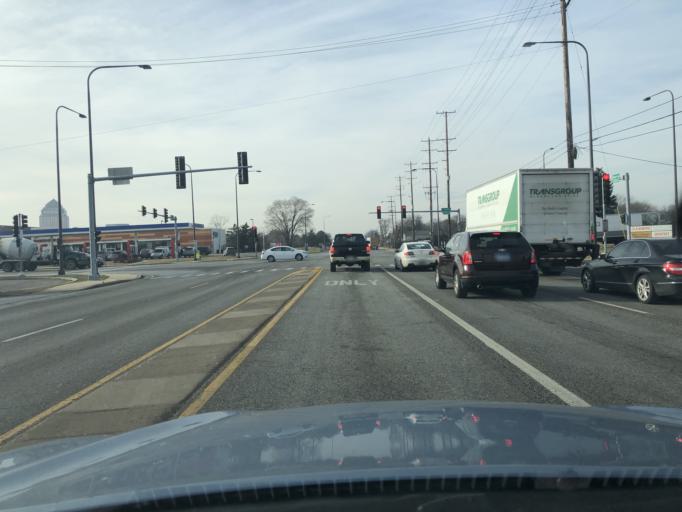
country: US
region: Illinois
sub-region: DuPage County
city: Itasca
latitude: 41.9926
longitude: -88.0024
